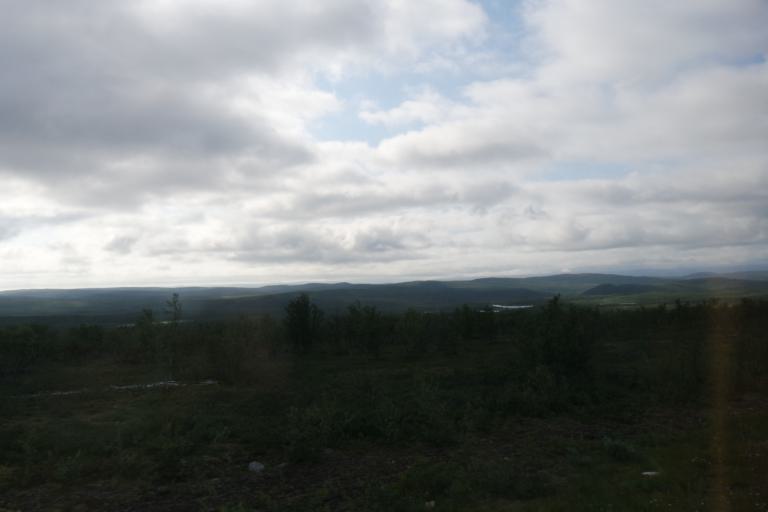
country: NO
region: Finnmark Fylke
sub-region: Karasjok
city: Karasjohka
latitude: 69.7189
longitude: 25.2382
